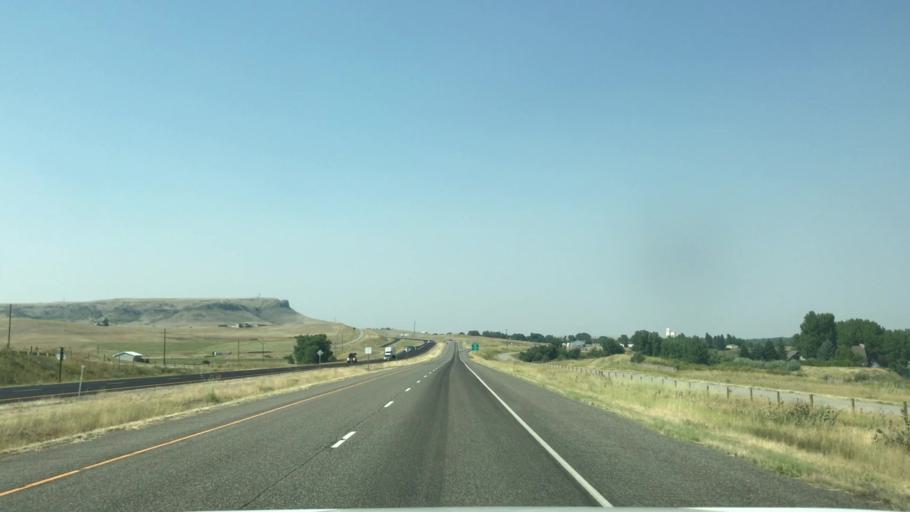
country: US
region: Montana
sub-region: Cascade County
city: Sun Prairie
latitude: 47.2524
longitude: -111.7100
